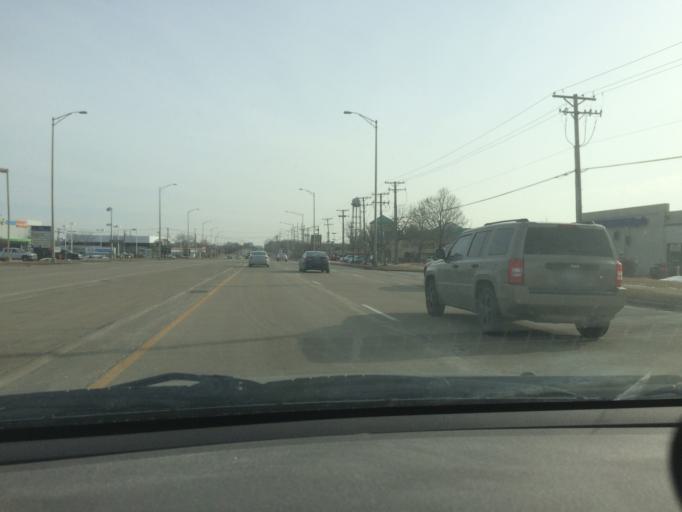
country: US
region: Illinois
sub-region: Cook County
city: Hoffman Estates
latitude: 42.0490
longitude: -88.0848
